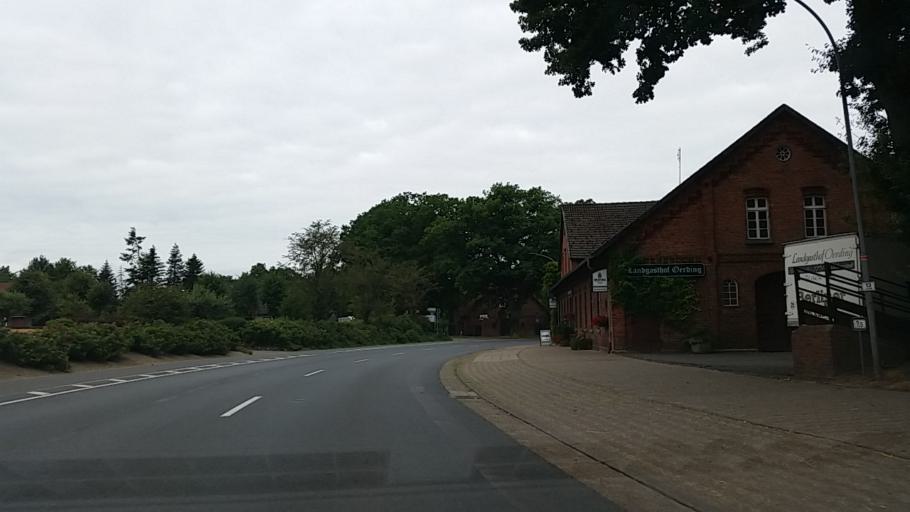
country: DE
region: Lower Saxony
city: Beverstedt
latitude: 53.4234
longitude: 8.8921
